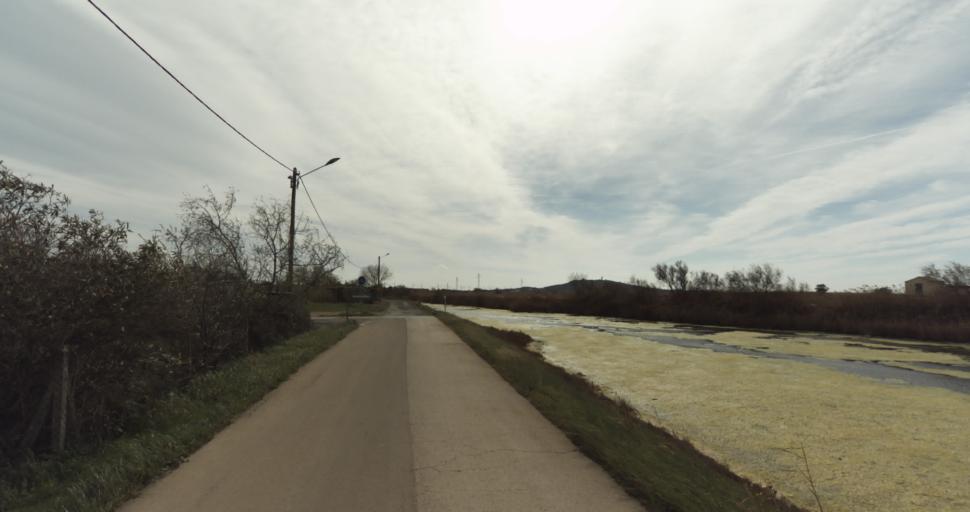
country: FR
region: Languedoc-Roussillon
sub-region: Departement de l'Herault
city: Marseillan
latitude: 43.3205
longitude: 3.5345
